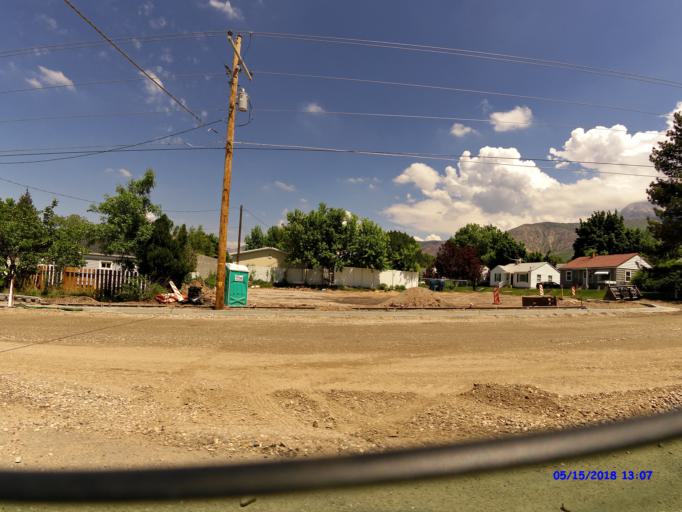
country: US
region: Utah
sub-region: Weber County
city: South Ogden
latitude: 41.1895
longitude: -111.9597
